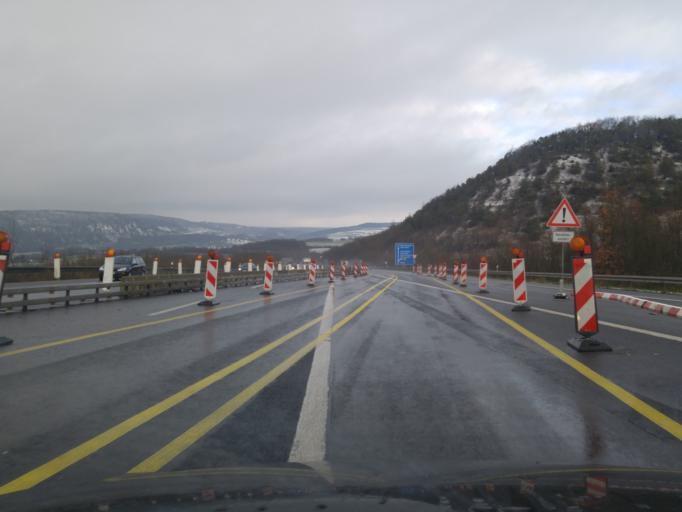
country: DE
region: Bavaria
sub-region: Regierungsbezirk Unterfranken
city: Fuchsstadt
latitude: 50.1170
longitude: 9.9580
